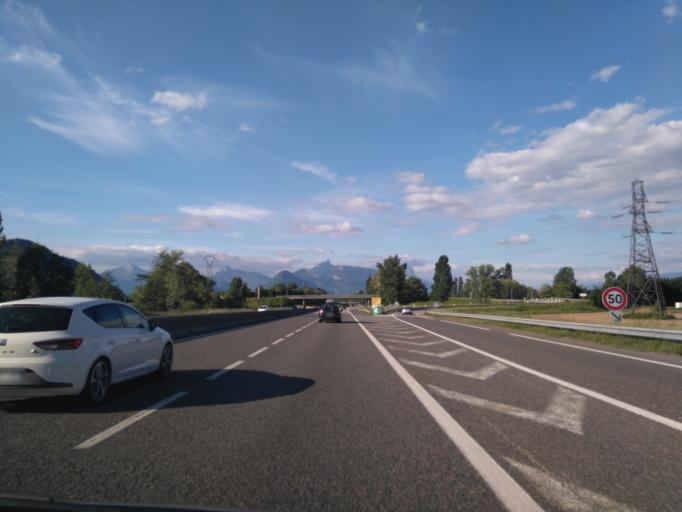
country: FR
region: Rhone-Alpes
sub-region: Departement de l'Isere
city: Claix
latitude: 45.1176
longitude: 5.6854
